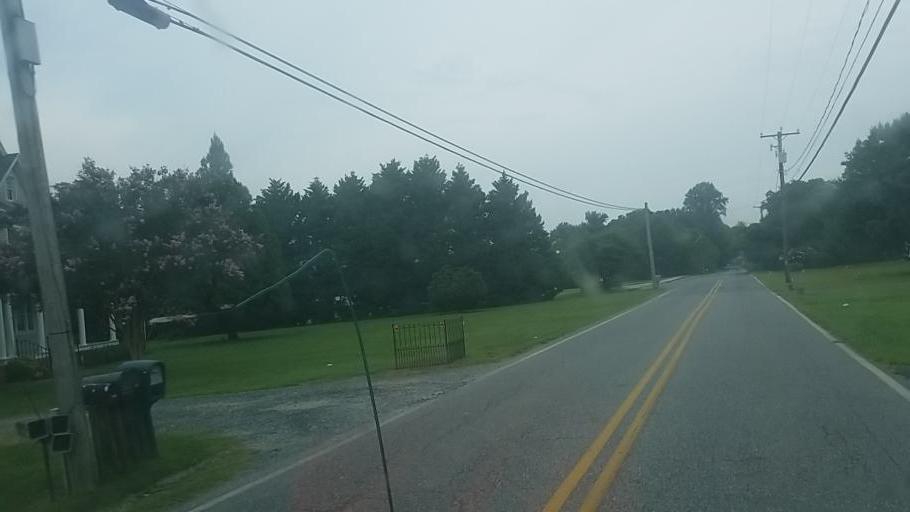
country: US
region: Maryland
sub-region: Wicomico County
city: Salisbury
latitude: 38.3716
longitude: -75.5492
